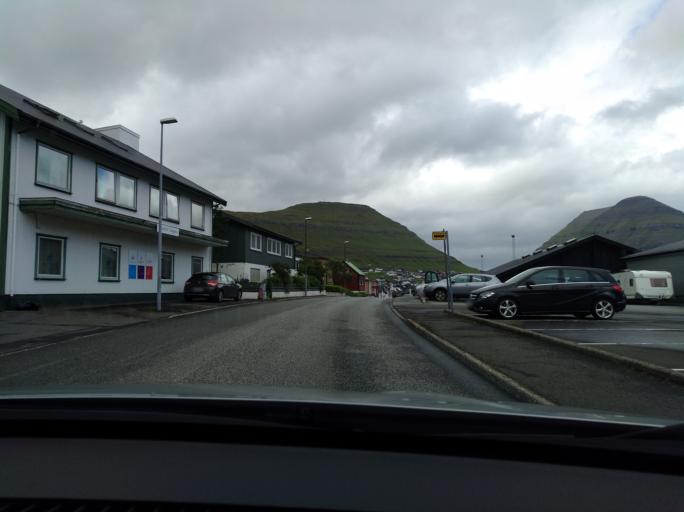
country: FO
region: Nordoyar
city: Klaksvik
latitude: 62.2234
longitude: -6.5789
